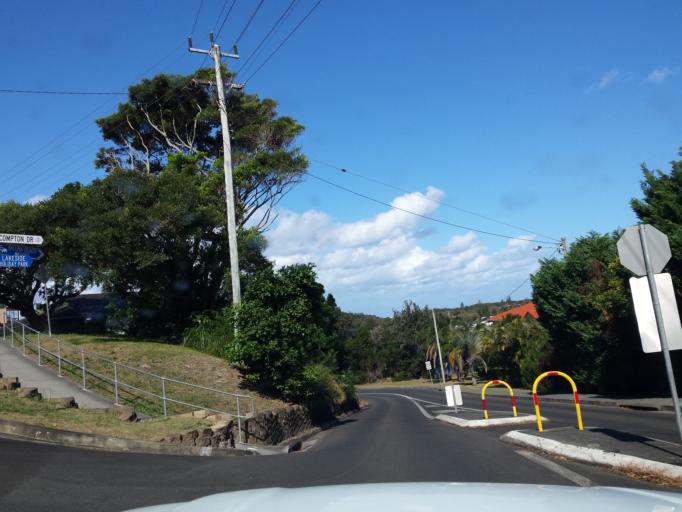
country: AU
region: New South Wales
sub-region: Ballina
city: East Ballina
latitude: -28.8659
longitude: 153.5802
